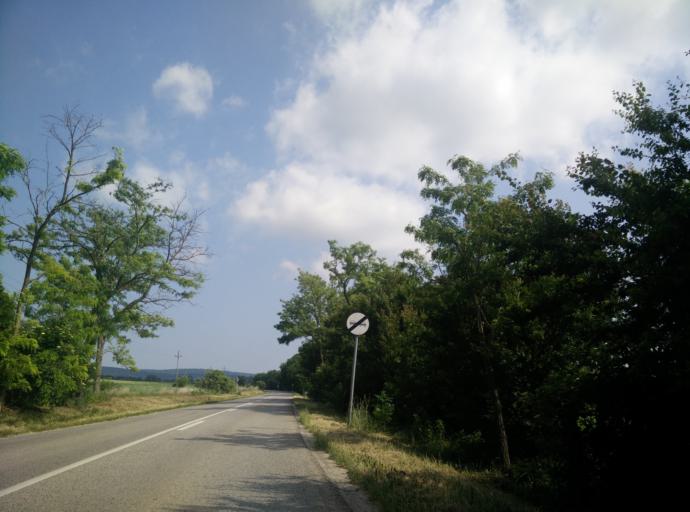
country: HU
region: Pest
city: Biatorbagy
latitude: 47.4771
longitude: 18.7919
